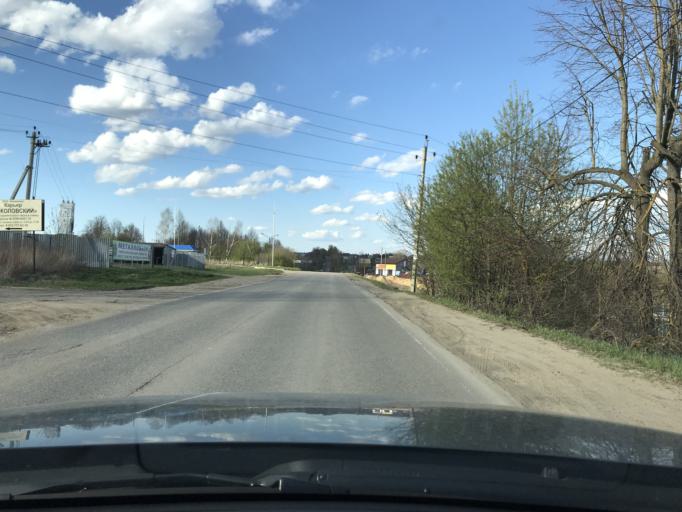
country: RU
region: Vladimir
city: Strunino
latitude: 56.3873
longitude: 38.5789
